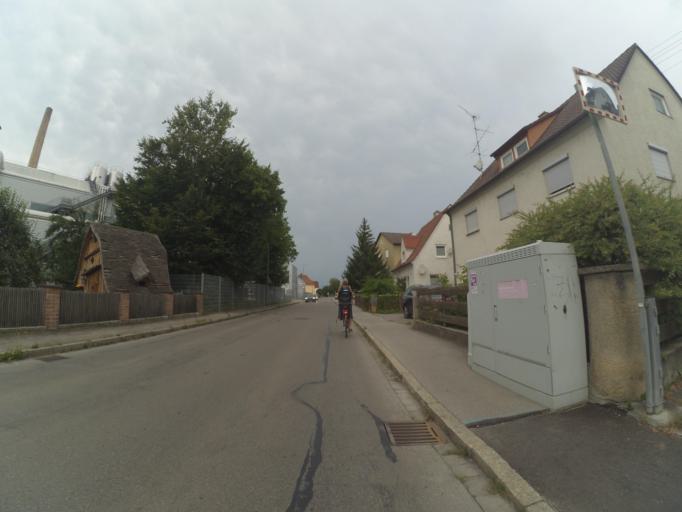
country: DE
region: Bavaria
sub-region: Swabia
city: Buchloe
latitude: 48.0379
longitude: 10.7167
